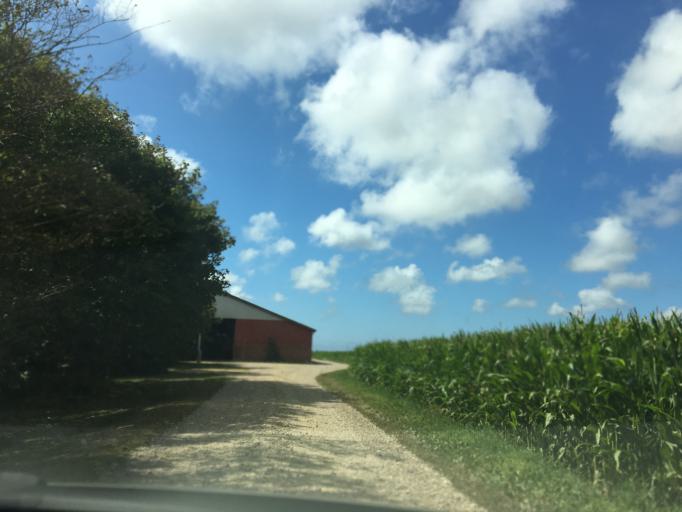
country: DK
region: South Denmark
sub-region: Varde Kommune
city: Oksbol
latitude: 55.8130
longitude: 8.2886
